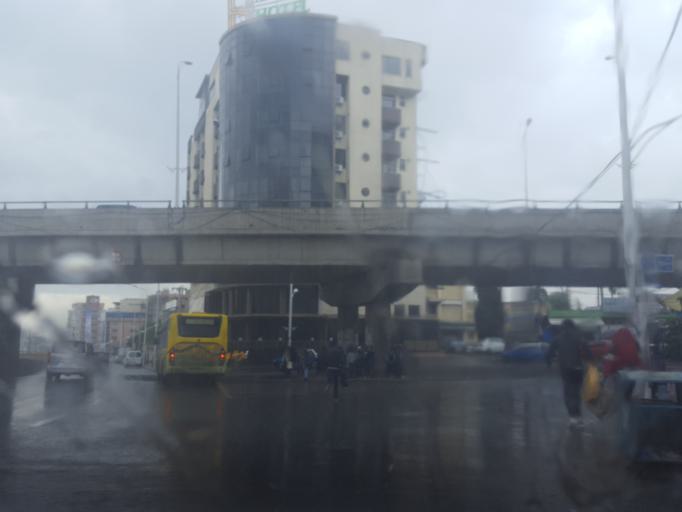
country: ET
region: Adis Abeba
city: Addis Ababa
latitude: 9.0146
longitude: 38.7821
